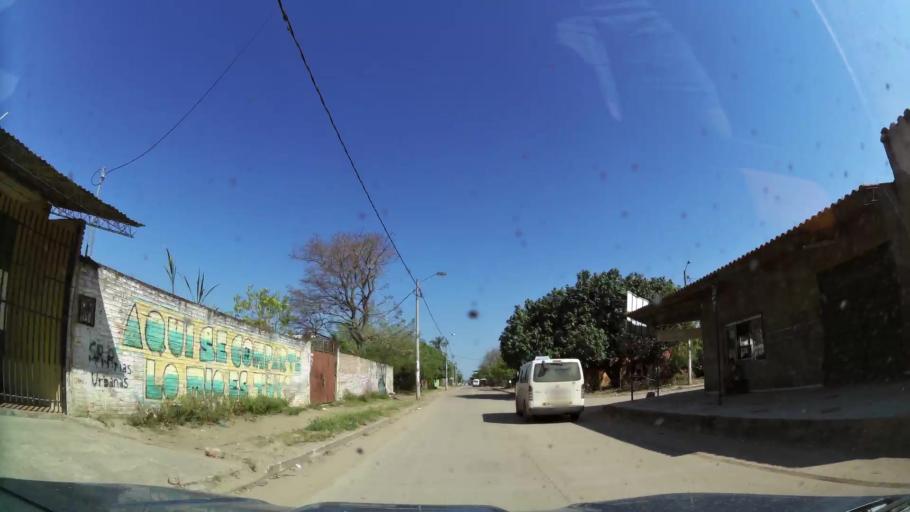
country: BO
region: Santa Cruz
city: Cotoca
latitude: -17.7359
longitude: -63.0741
